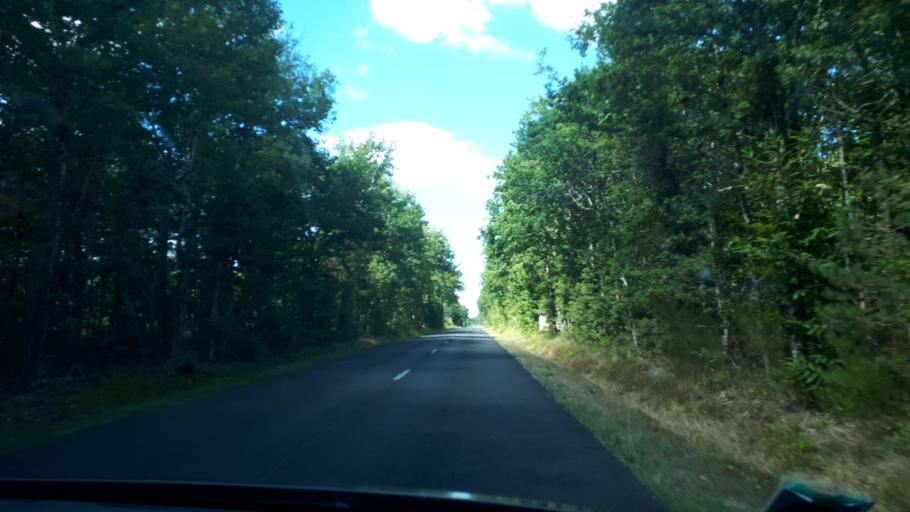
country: FR
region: Centre
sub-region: Departement du Loir-et-Cher
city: Dhuizon
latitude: 47.5344
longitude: 1.7099
